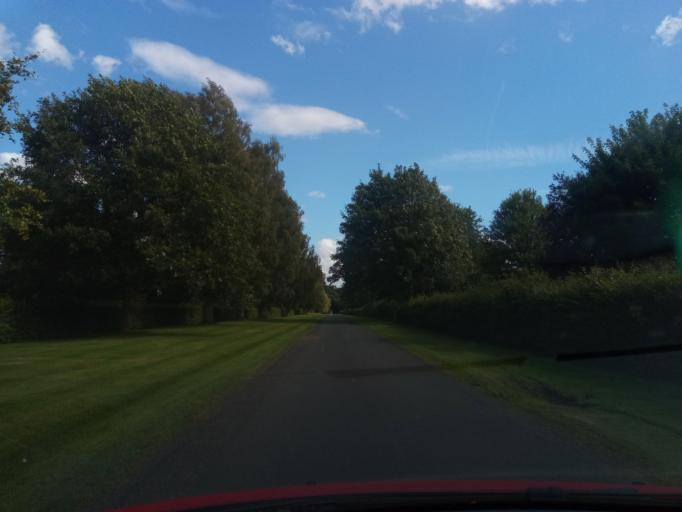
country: GB
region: Scotland
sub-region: The Scottish Borders
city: Coldstream
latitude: 55.6513
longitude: -2.2689
